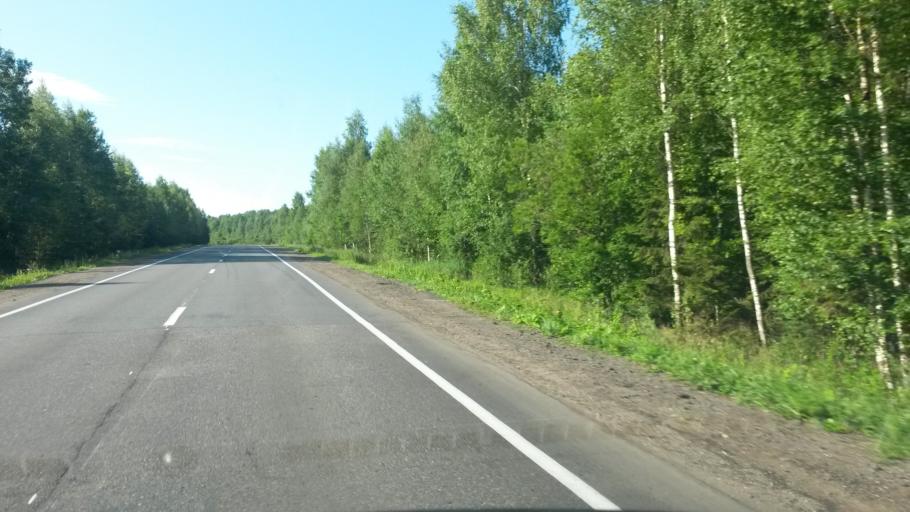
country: RU
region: Jaroslavl
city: Gavrilov-Yam
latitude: 57.2959
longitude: 39.9493
